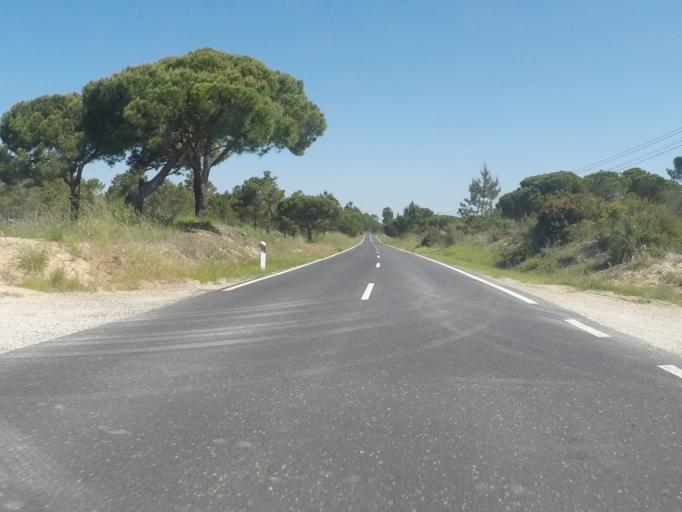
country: PT
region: Setubal
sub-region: Grandola
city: Grandola
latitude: 38.2820
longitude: -8.7258
